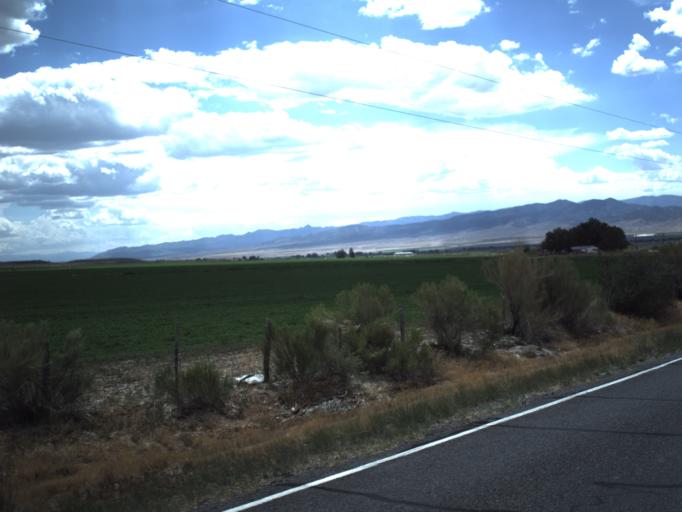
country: US
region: Utah
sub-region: Sanpete County
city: Gunnison
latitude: 39.1445
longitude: -111.7589
